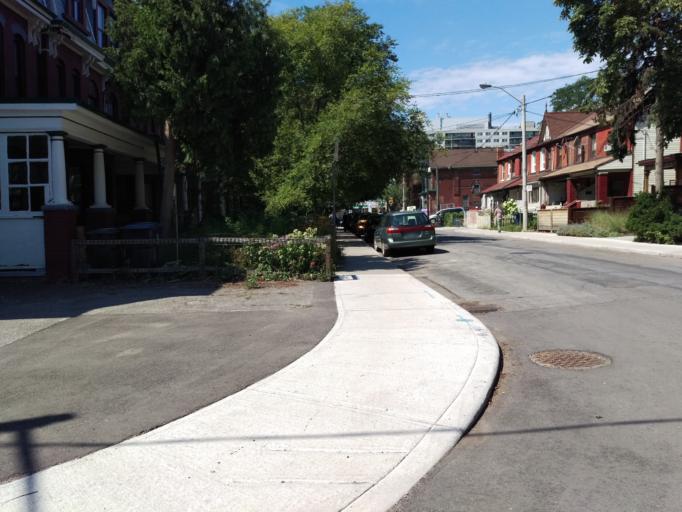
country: CA
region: Ontario
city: Toronto
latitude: 43.6512
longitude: -79.3954
